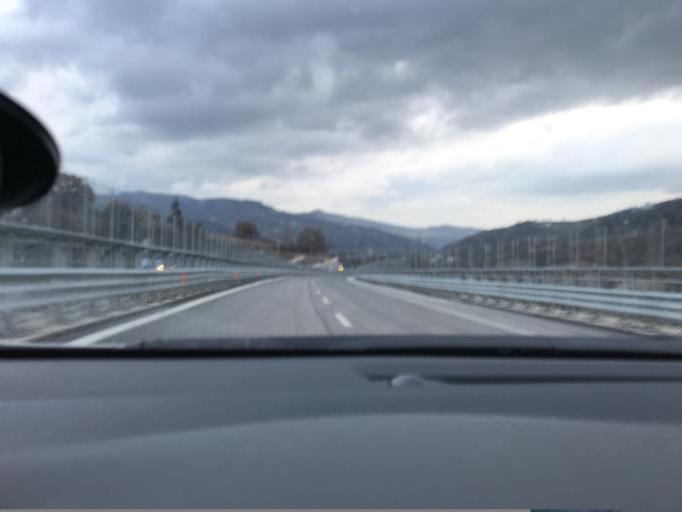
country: IT
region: Umbria
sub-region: Provincia di Perugia
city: Valfabbrica
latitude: 43.1726
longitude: 12.6029
